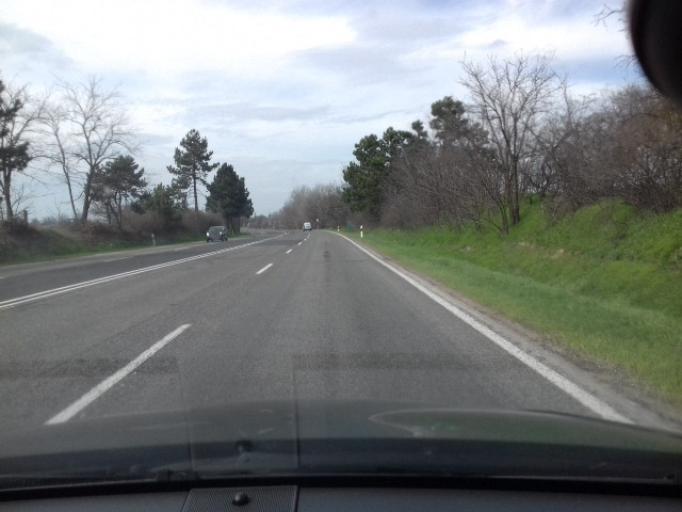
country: HU
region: Bacs-Kiskun
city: Kecskemet
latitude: 46.9546
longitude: 19.6484
